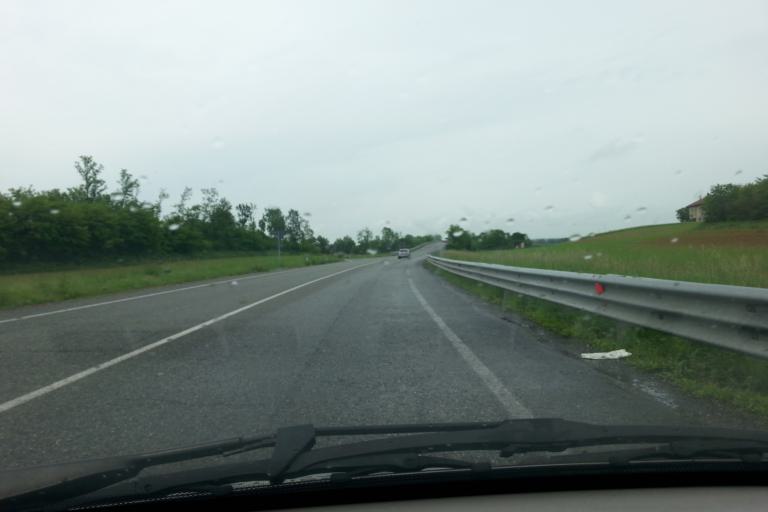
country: IT
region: Piedmont
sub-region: Provincia di Torino
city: Alpignano
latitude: 45.1165
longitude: 7.5141
